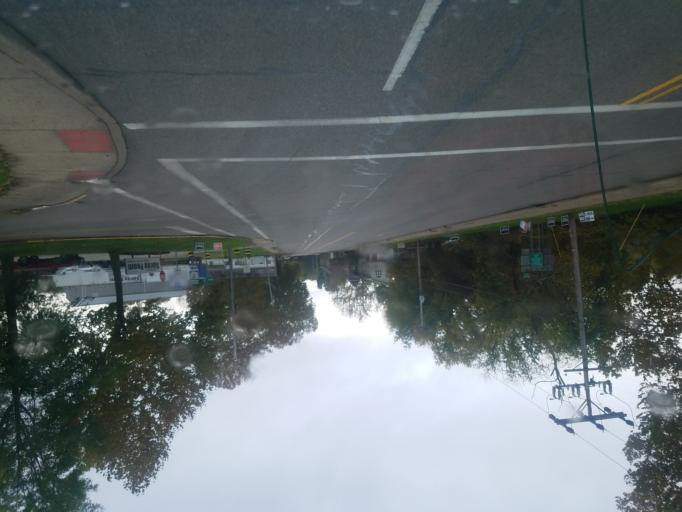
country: US
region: Ohio
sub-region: Washington County
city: Marietta
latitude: 39.4182
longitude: -81.4634
